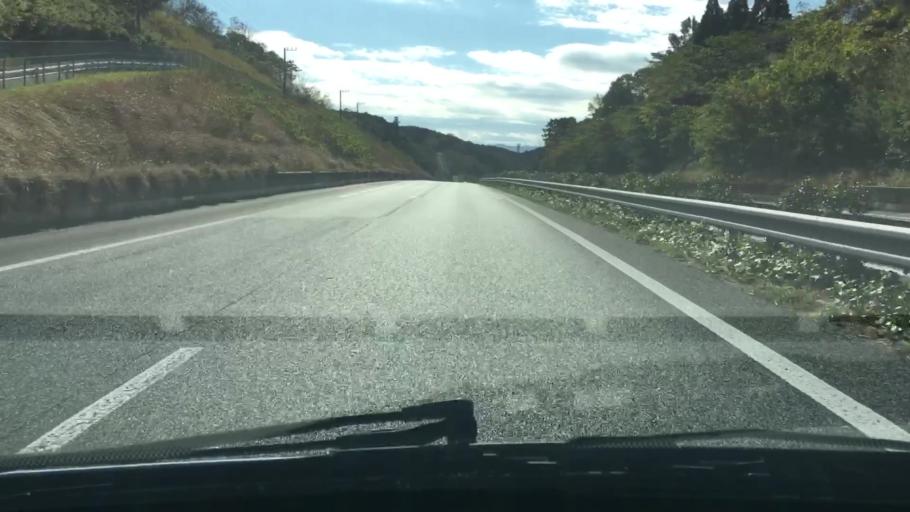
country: JP
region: Chiba
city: Kisarazu
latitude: 35.3328
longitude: 139.9455
